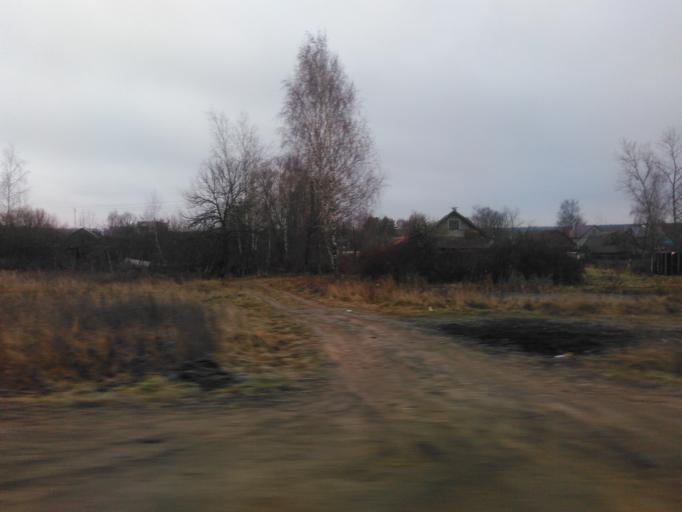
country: RU
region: Moskovskaya
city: Ashukino
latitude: 56.1762
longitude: 37.9366
